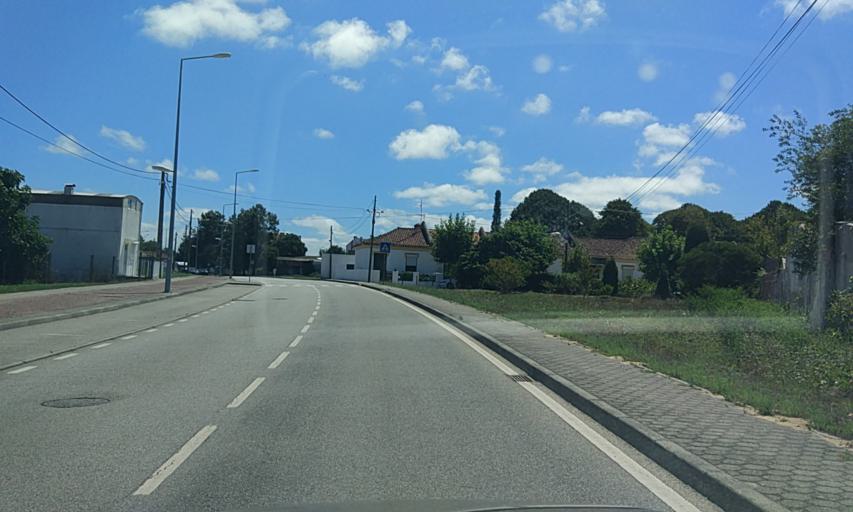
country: PT
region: Aveiro
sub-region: Ilhavo
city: Ilhavo
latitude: 40.5897
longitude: -8.6806
